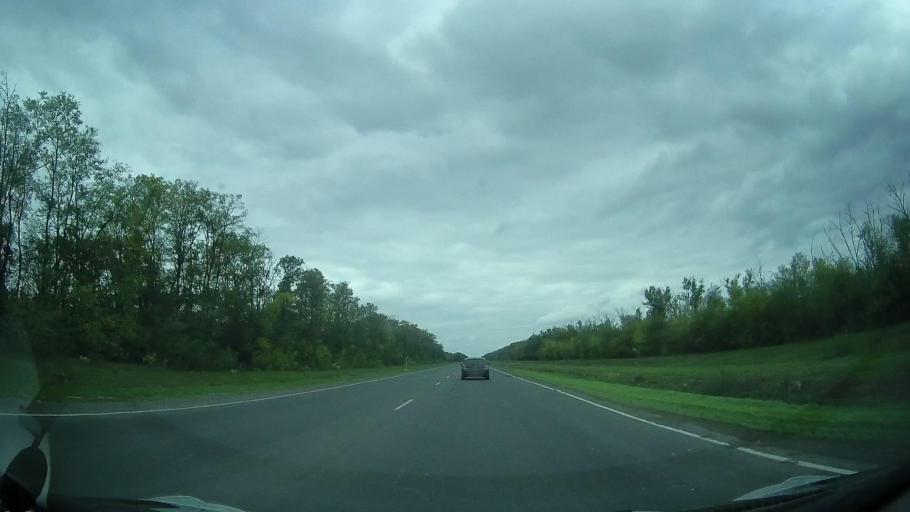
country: RU
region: Rostov
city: Yegorlykskaya
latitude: 46.5967
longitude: 40.6224
